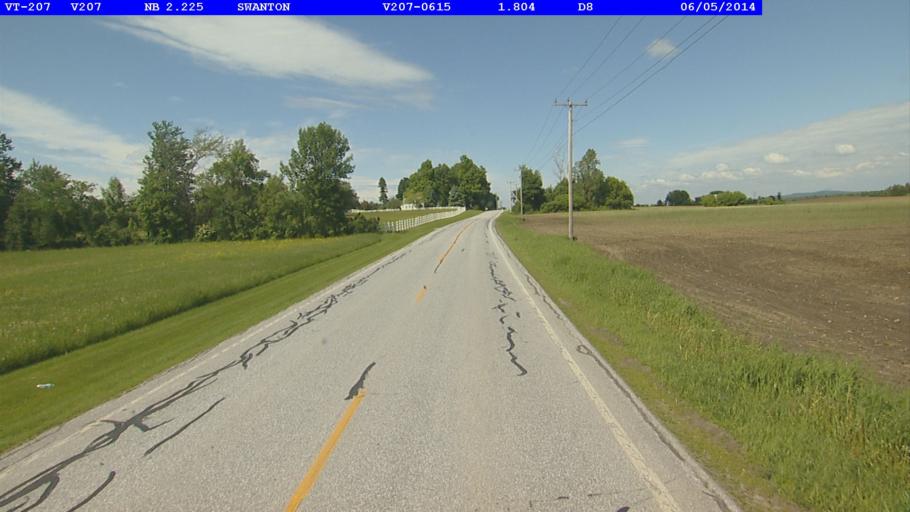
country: US
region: Vermont
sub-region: Franklin County
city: Saint Albans
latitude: 44.8710
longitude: -73.0753
